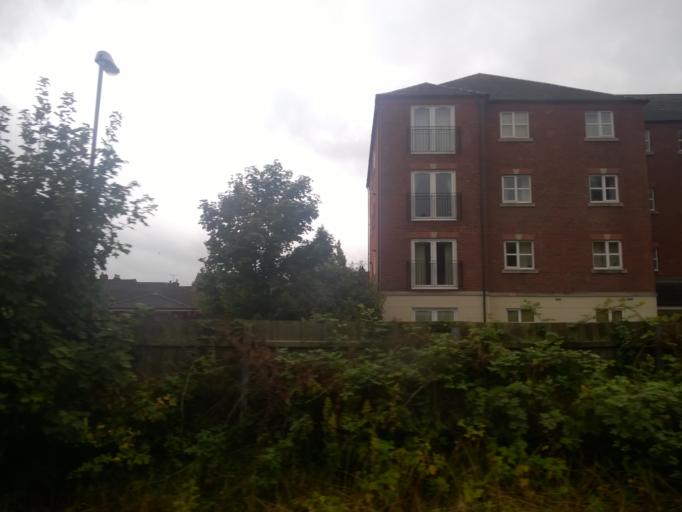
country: GB
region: England
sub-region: Worcestershire
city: Worcester
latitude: 52.1907
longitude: -2.2361
